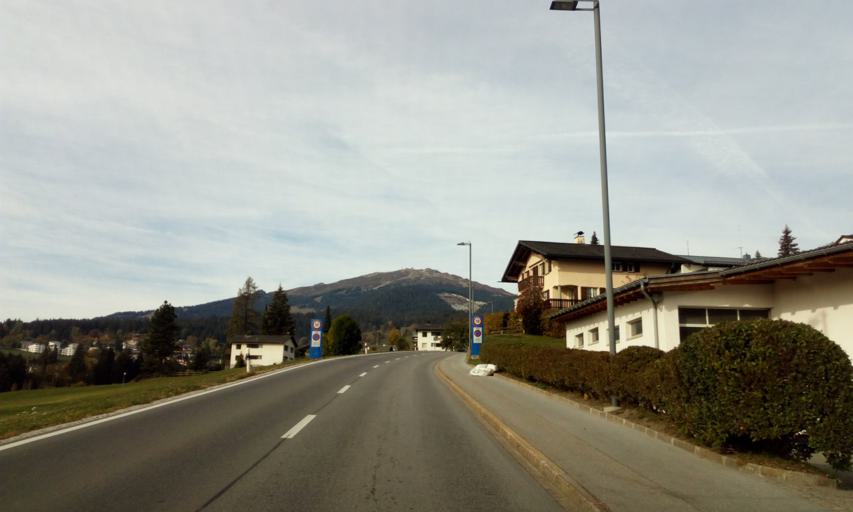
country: CH
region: Grisons
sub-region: Imboden District
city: Flims
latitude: 46.8351
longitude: 9.2995
